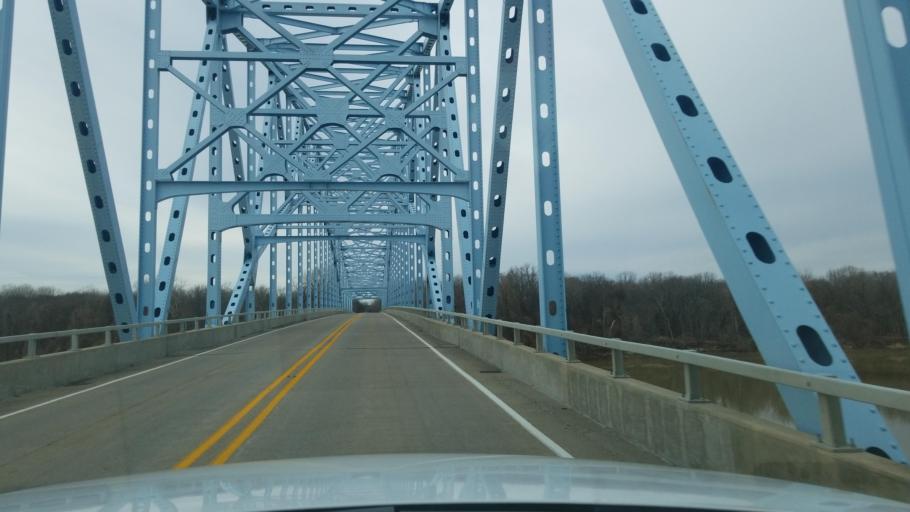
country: US
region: Indiana
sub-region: Posey County
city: Mount Vernon
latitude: 37.9440
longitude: -88.0349
